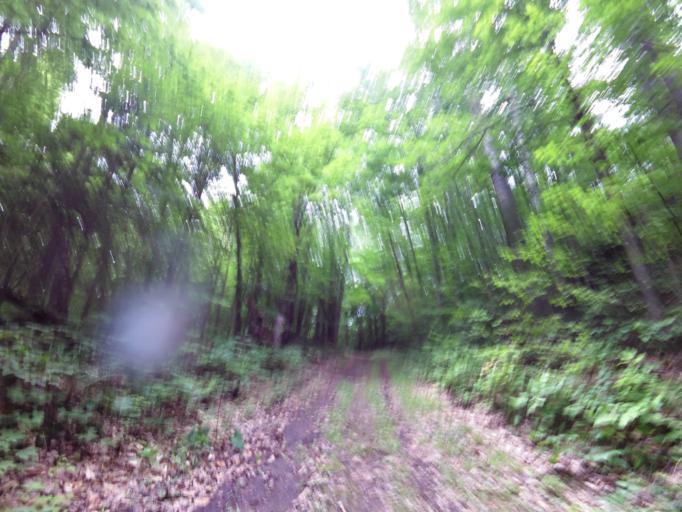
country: CA
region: Quebec
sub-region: Outaouais
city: Wakefield
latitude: 45.6147
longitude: -76.0455
